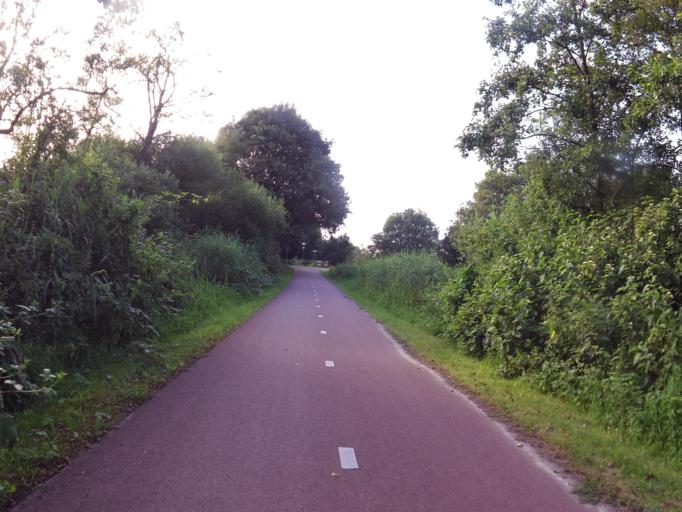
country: NL
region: North Brabant
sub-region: Gemeente Geldrop-Mierlo
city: Geldrop
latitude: 51.4340
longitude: 5.5490
